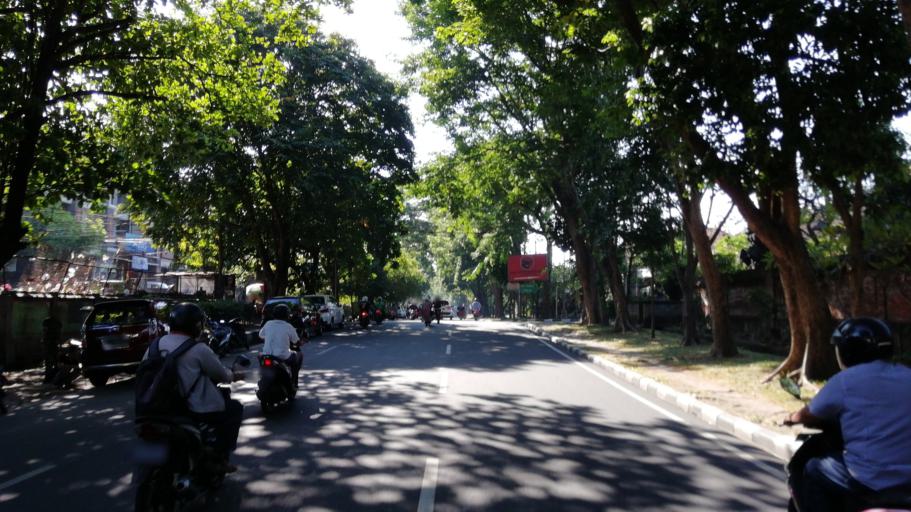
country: ID
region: Bali
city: Denpasar
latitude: -8.6669
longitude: 115.2249
